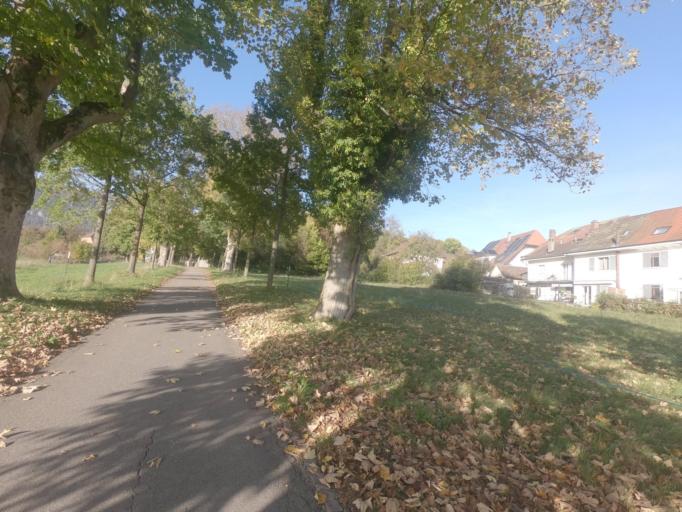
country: CH
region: Solothurn
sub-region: Bezirk Solothurn
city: Solothurn
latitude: 47.2185
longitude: 7.5284
